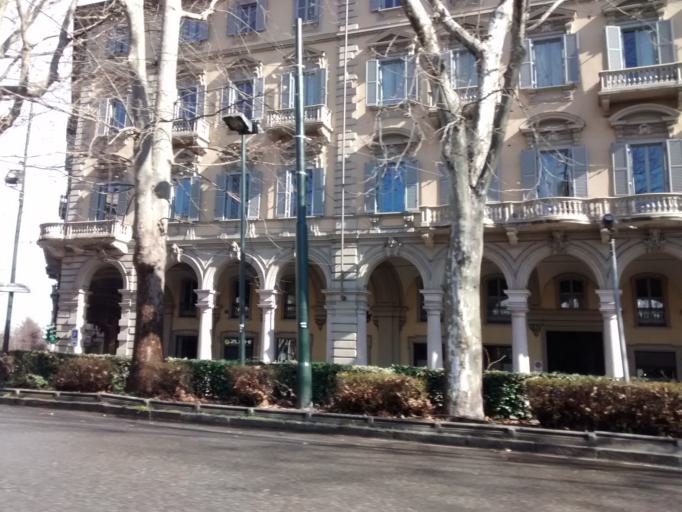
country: IT
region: Piedmont
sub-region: Provincia di Torino
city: Turin
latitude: 45.0657
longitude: 7.6713
